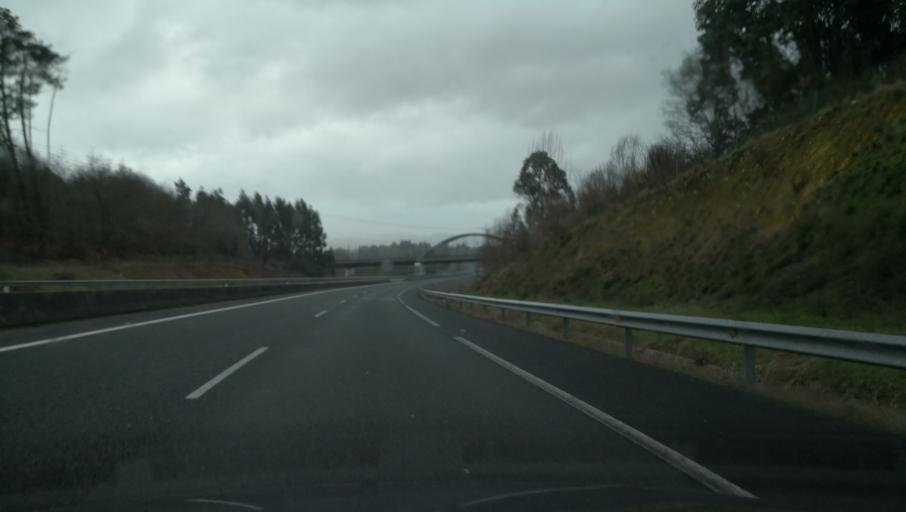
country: ES
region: Galicia
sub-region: Provincia de Pontevedra
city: Lalin
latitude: 42.6880
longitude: -8.1724
